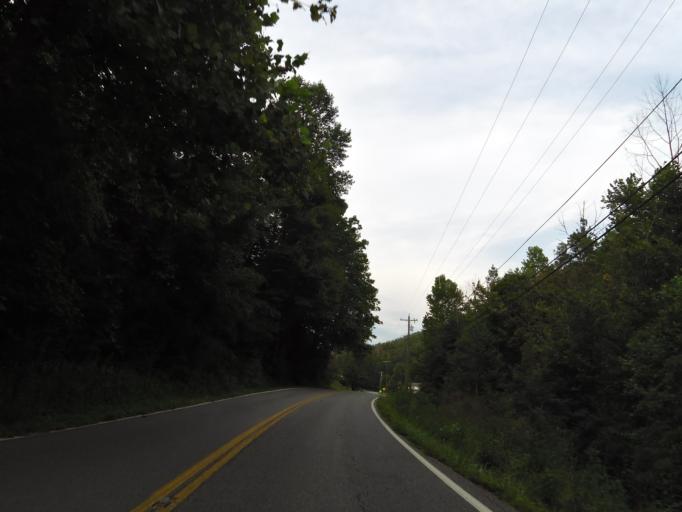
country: US
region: Tennessee
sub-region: Anderson County
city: Clinton
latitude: 36.1306
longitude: -84.2203
